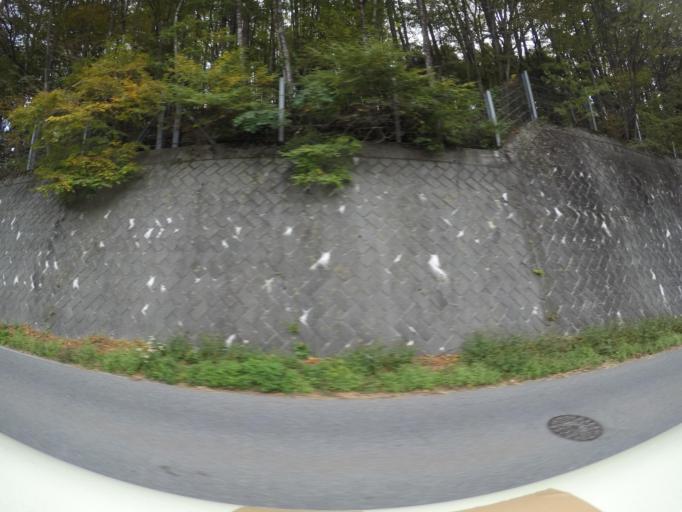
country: JP
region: Nagano
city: Chino
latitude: 35.8701
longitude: 138.0923
